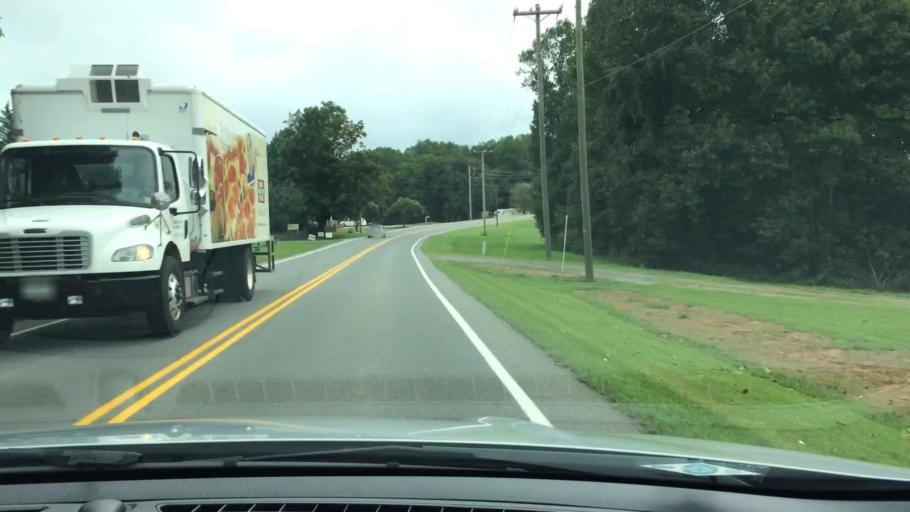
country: US
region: Virginia
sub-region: Franklin County
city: Henry Fork
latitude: 37.0098
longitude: -79.7843
